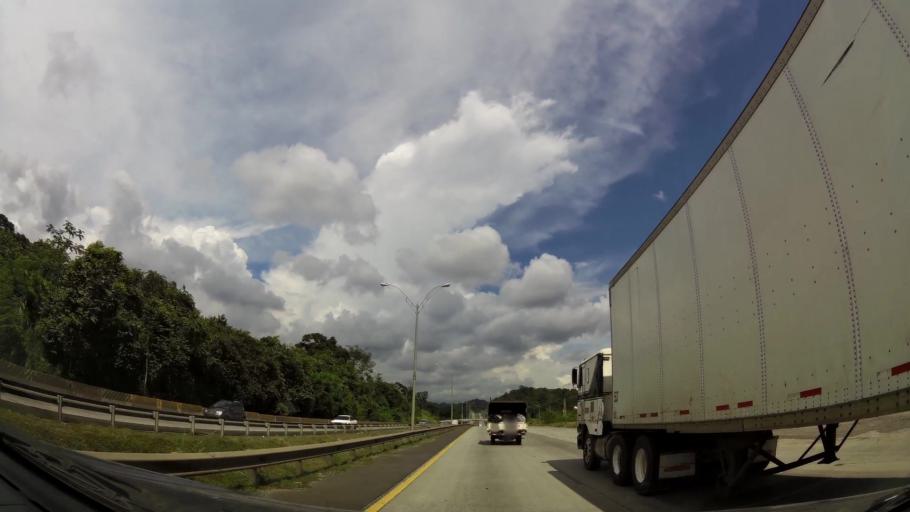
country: PA
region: Panama
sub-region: Distrito de Panama
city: Paraiso
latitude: 9.0325
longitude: -79.5817
